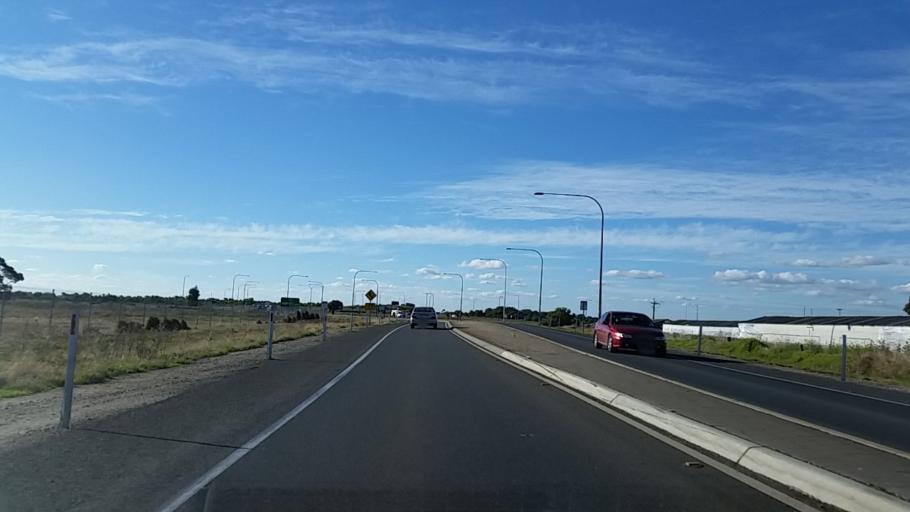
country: AU
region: South Australia
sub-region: Playford
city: Angle Vale
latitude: -34.6847
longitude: 138.6207
